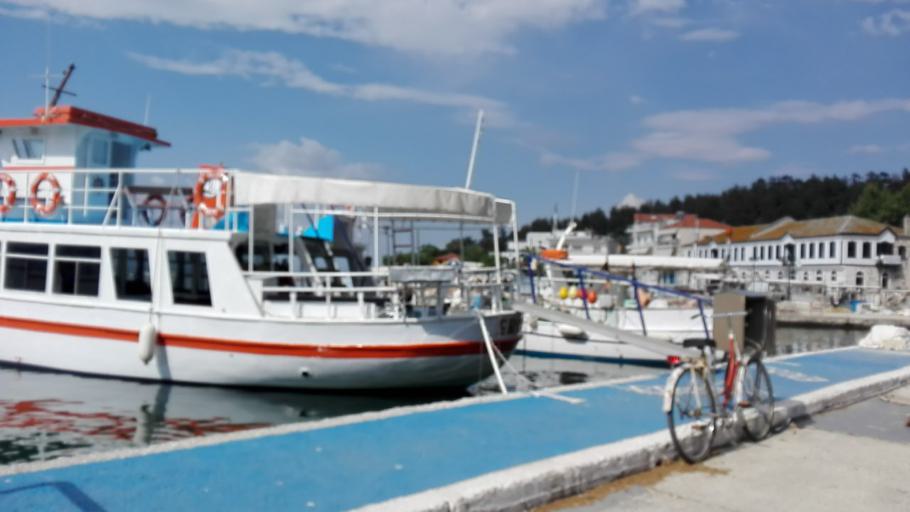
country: GR
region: East Macedonia and Thrace
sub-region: Nomos Kavalas
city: Thasos
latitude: 40.7806
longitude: 24.7126
